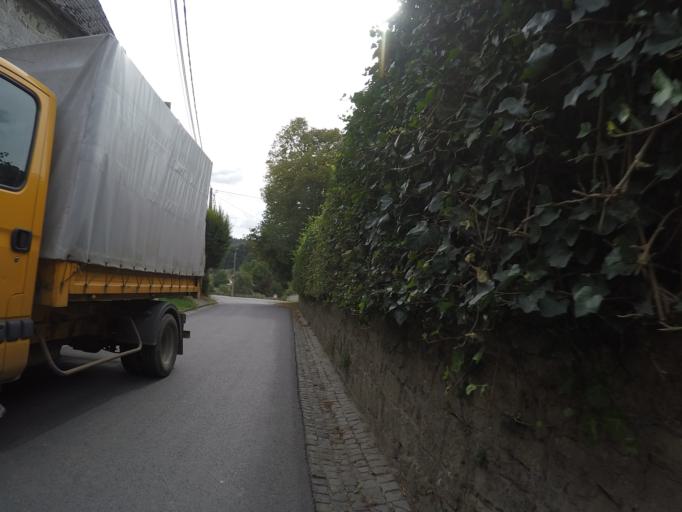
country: BE
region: Wallonia
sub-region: Province de Namur
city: Dinant
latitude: 50.2798
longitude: 4.9868
